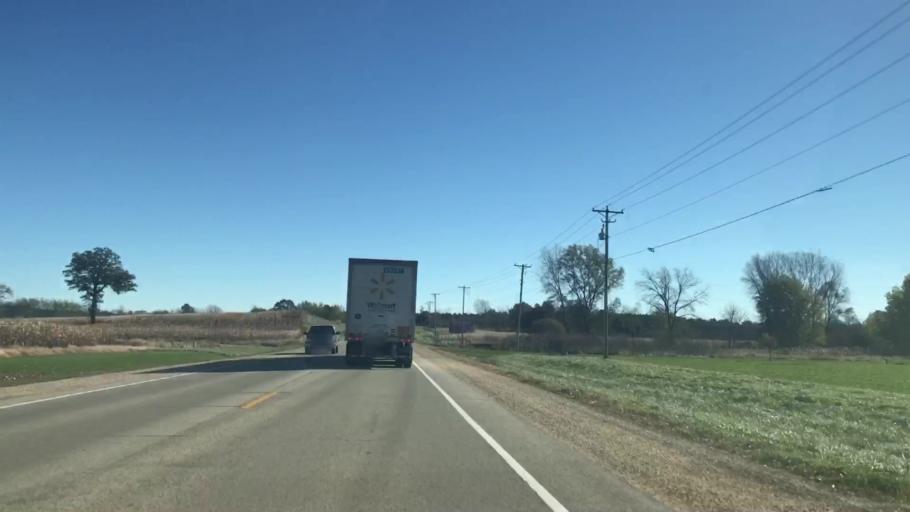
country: US
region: Wisconsin
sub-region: Dodge County
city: Juneau
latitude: 43.4448
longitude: -88.7166
